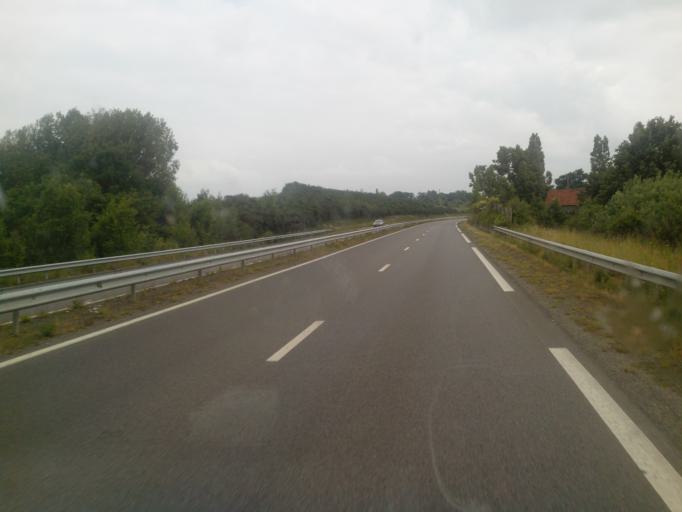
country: FR
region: Brittany
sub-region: Departement d'Ille-et-Vilaine
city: Chevaigne
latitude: 48.2039
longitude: -1.6218
